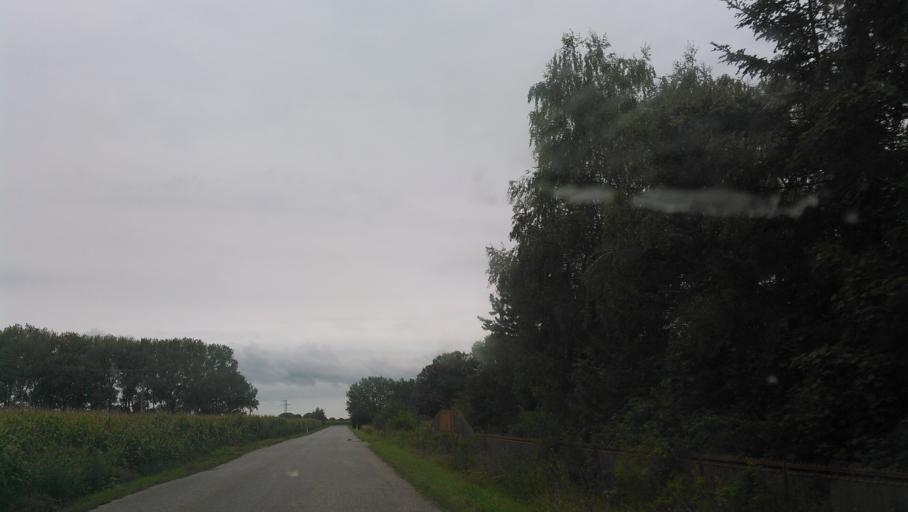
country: SK
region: Trnavsky
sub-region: Okres Dunajska Streda
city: Velky Meder
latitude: 47.9041
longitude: 17.8724
